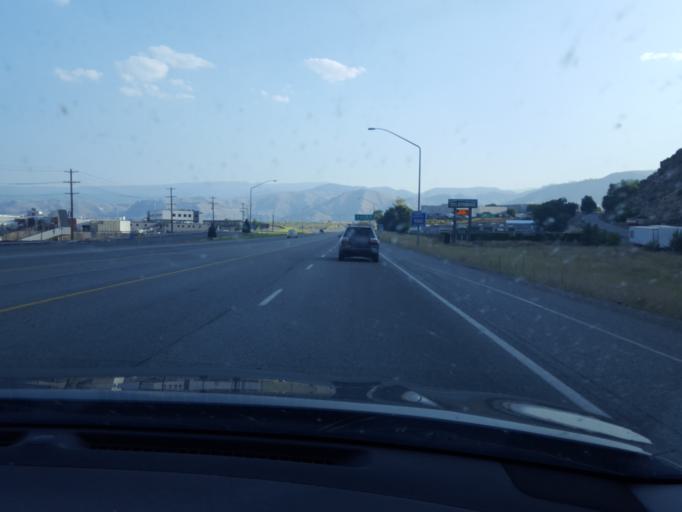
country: US
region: Washington
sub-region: Chelan County
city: Sunnyslope
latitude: 47.4791
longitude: -120.3222
